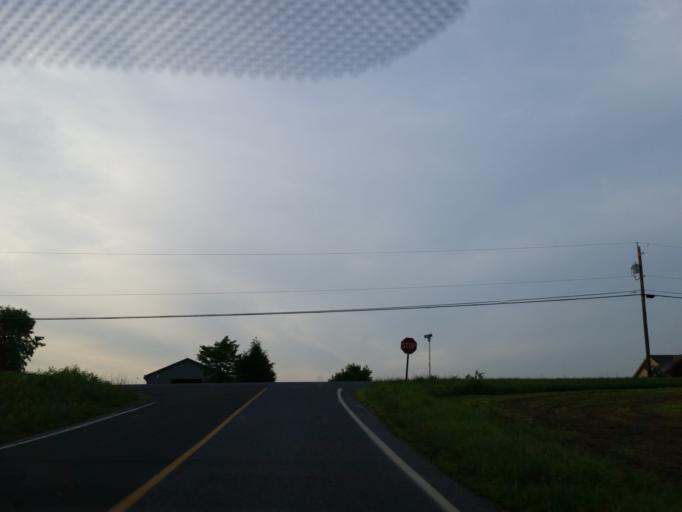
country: US
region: Pennsylvania
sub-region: Lebanon County
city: Jonestown
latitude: 40.4180
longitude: -76.5142
